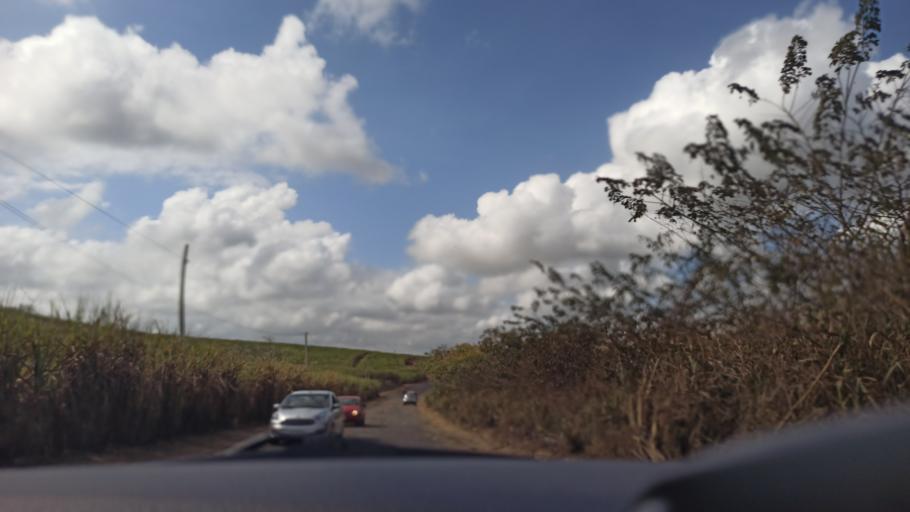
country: BR
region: Paraiba
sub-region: Juripiranga
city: Juripiranga
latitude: -7.4010
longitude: -35.2579
